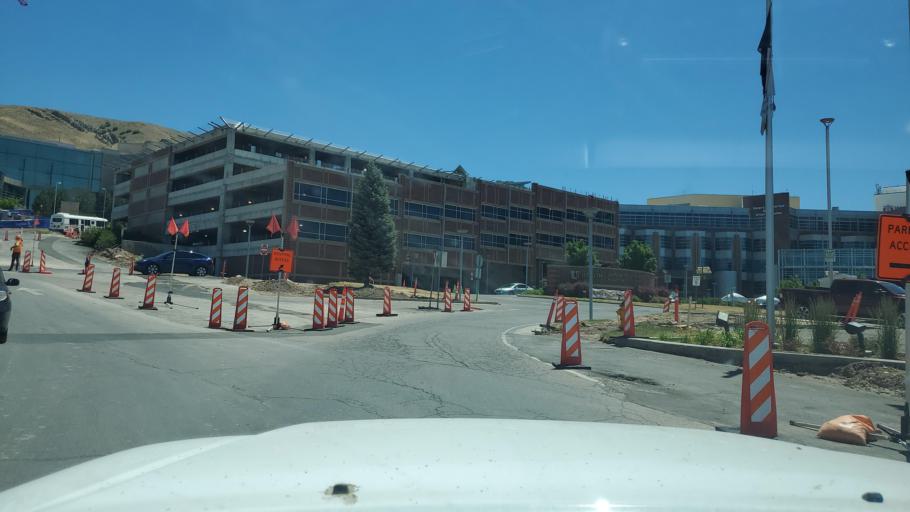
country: US
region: Utah
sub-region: Salt Lake County
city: Salt Lake City
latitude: 40.7725
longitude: -111.8384
